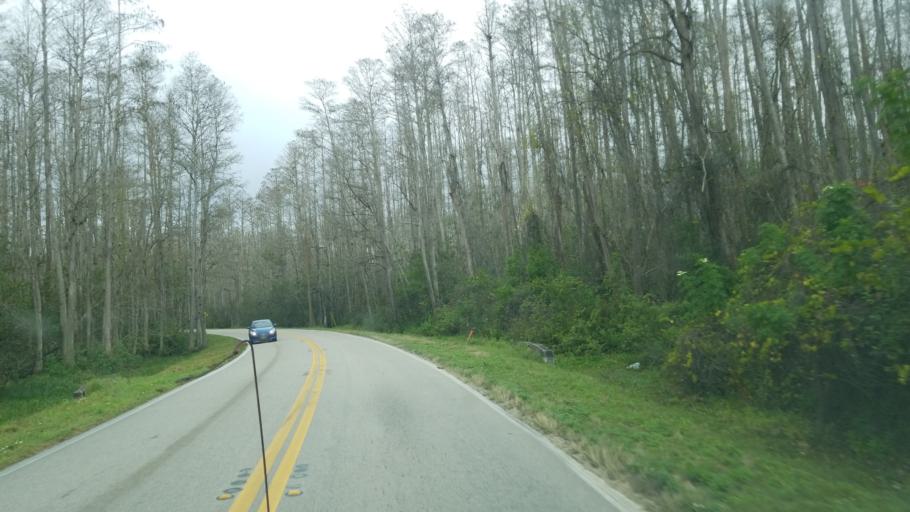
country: US
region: Florida
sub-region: Lake County
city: Four Corners
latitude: 28.2590
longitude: -81.7111
